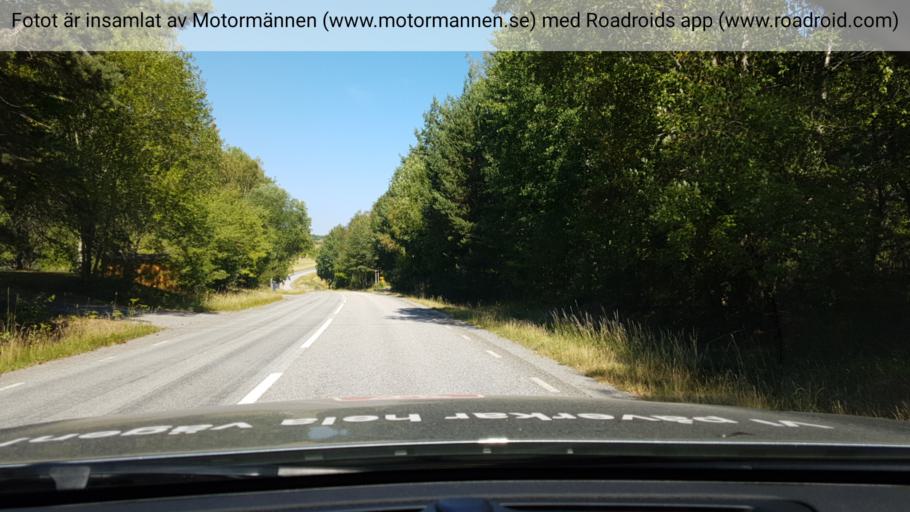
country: SE
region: Stockholm
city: Stenhamra
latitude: 59.3889
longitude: 17.5761
